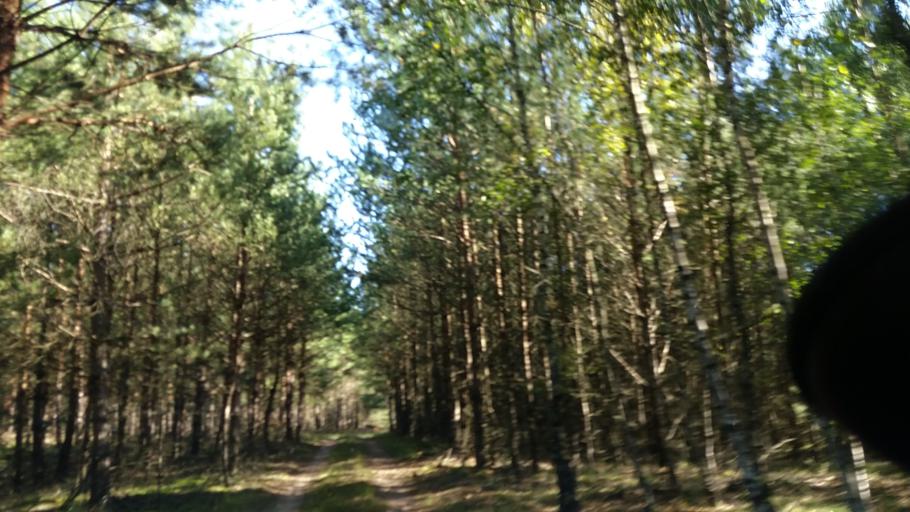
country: PL
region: West Pomeranian Voivodeship
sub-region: Powiat szczecinecki
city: Borne Sulinowo
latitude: 53.5774
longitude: 16.5183
